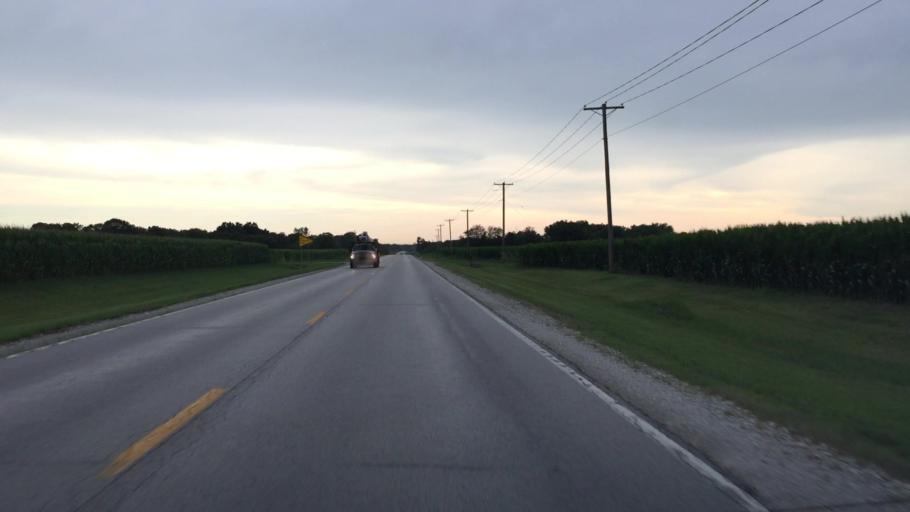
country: US
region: Illinois
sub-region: Hancock County
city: Hamilton
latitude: 40.3624
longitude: -91.3505
